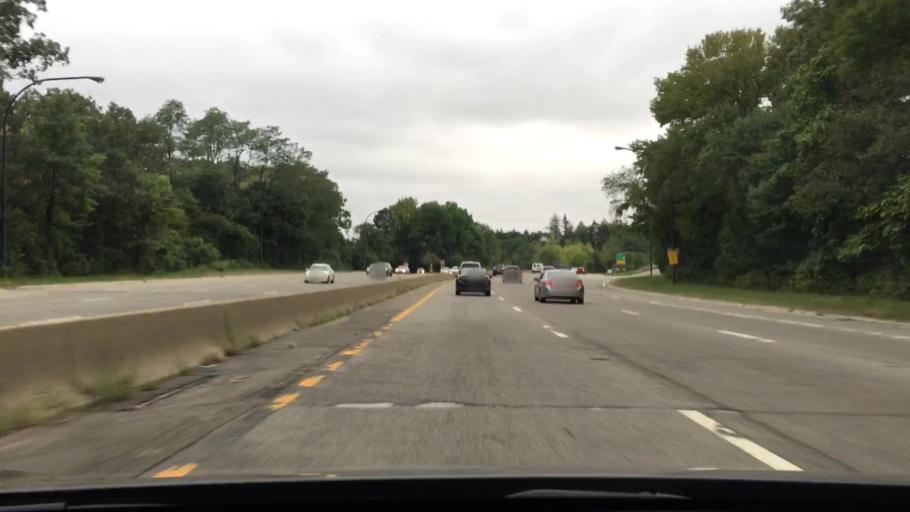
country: US
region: New York
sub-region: Nassau County
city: North Hills
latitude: 40.7757
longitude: -73.6669
